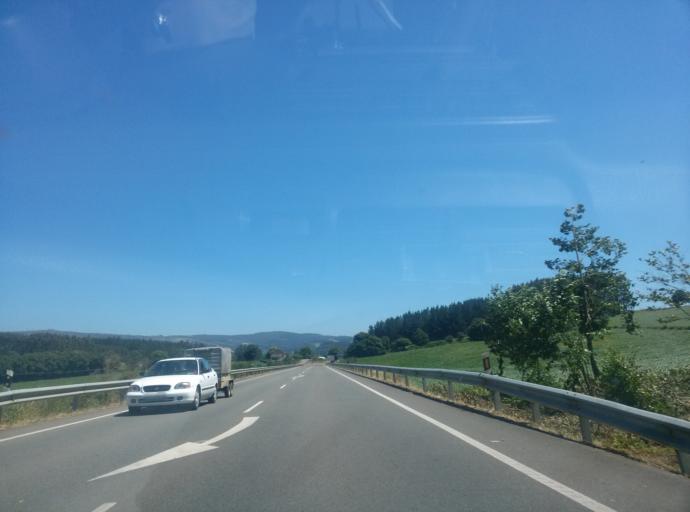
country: ES
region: Galicia
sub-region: Provincia de Lugo
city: Meira
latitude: 43.2297
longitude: -7.3348
